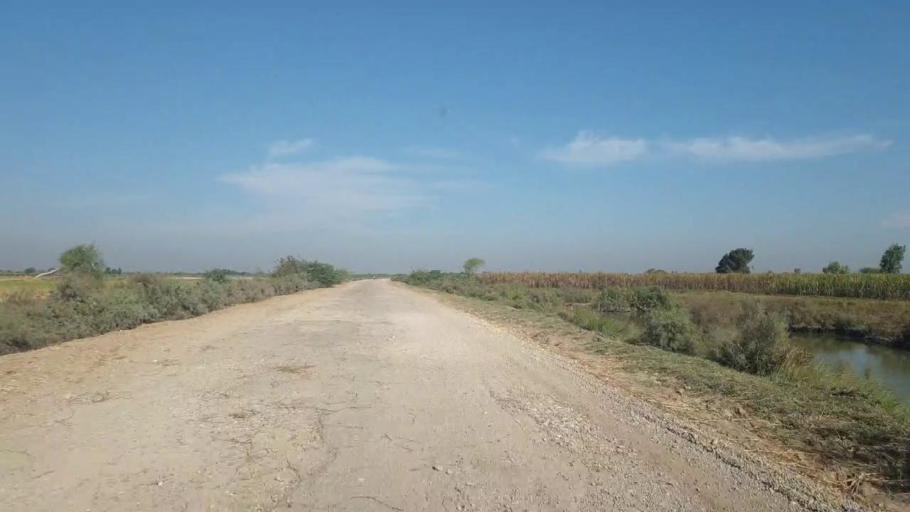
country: PK
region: Sindh
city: Talhar
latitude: 24.9173
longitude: 68.8027
